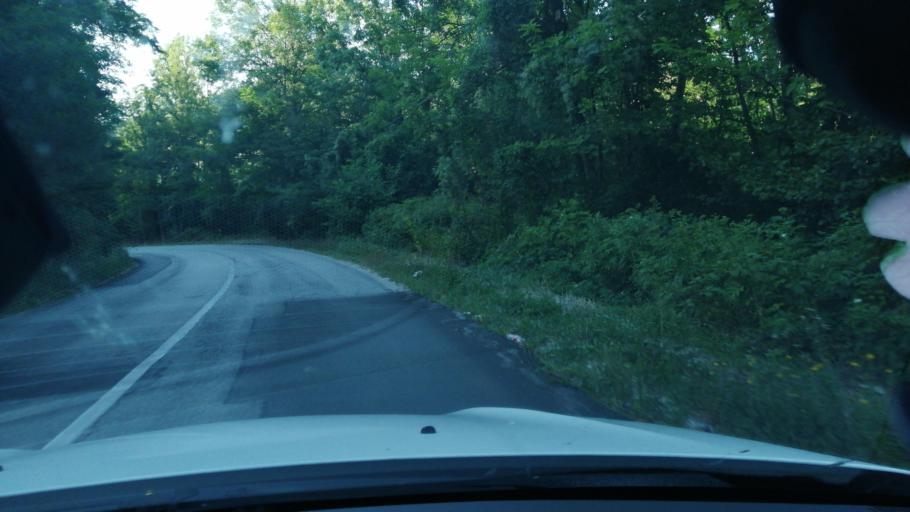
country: RS
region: Central Serbia
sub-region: Moravicki Okrug
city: Ivanjica
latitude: 43.6735
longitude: 20.2625
